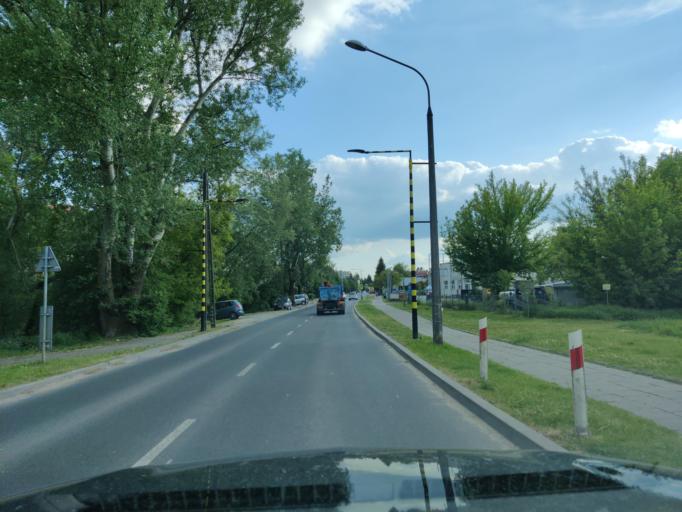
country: PL
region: Masovian Voivodeship
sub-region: Powiat piaseczynski
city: Konstancin-Jeziorna
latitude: 52.0979
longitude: 21.1246
